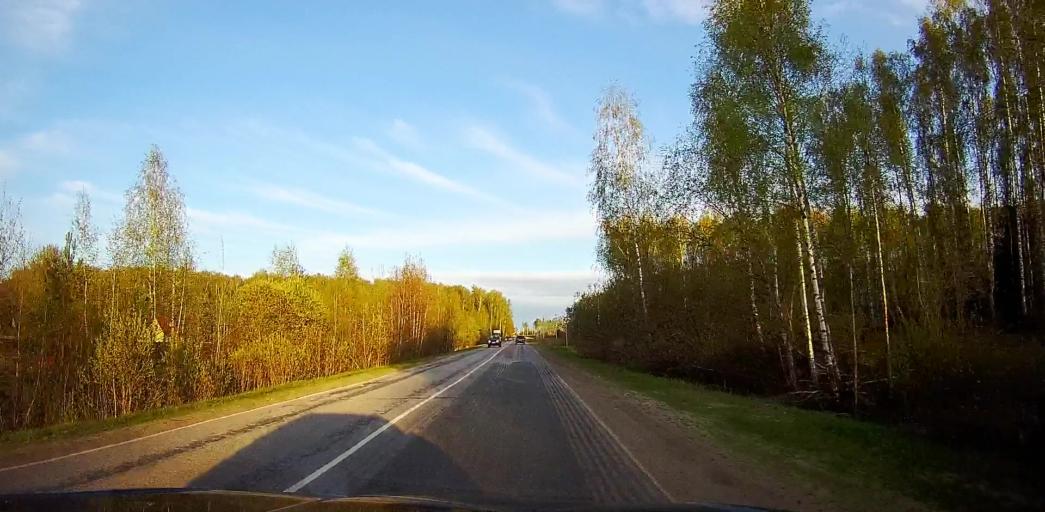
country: RU
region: Moskovskaya
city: Meshcherino
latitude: 55.2259
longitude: 38.3924
